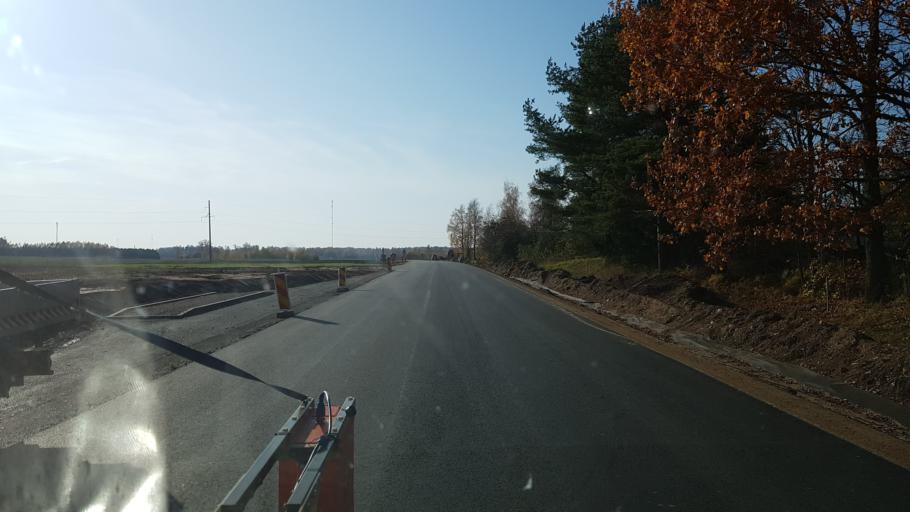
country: EE
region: Vorumaa
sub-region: Antsla vald
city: Vana-Antsla
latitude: 57.8441
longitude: 26.5591
